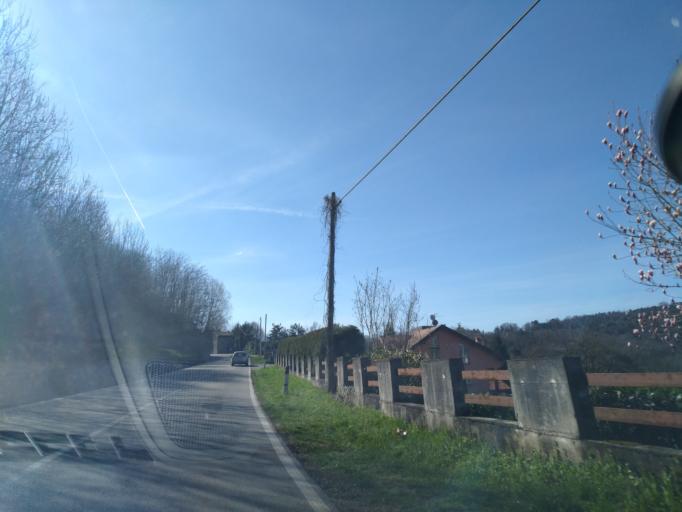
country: IT
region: Lombardy
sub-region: Provincia di Como
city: Montorfano
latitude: 45.7881
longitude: 9.1333
